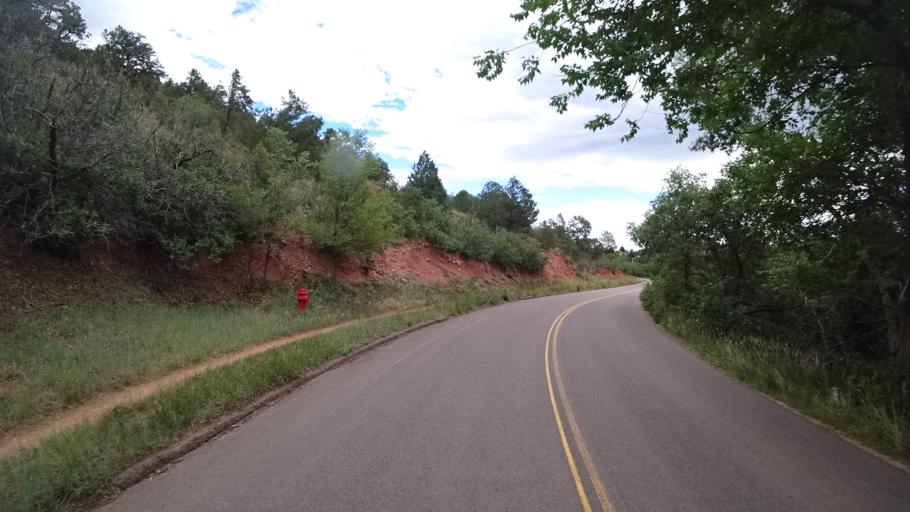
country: US
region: Colorado
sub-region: El Paso County
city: Manitou Springs
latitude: 38.8445
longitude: -104.9021
